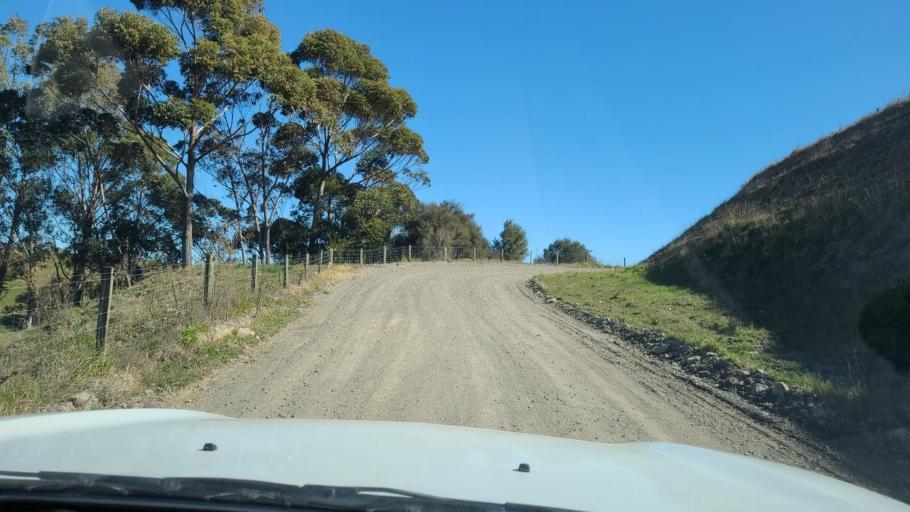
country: NZ
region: Hawke's Bay
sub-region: Napier City
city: Taradale
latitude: -39.4393
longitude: 176.5564
